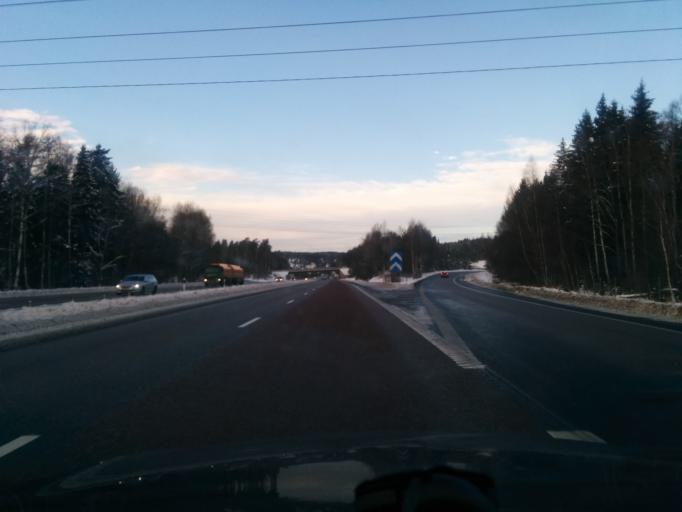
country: SE
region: Uppsala
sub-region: Habo Kommun
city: Balsta
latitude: 59.5638
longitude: 17.5663
